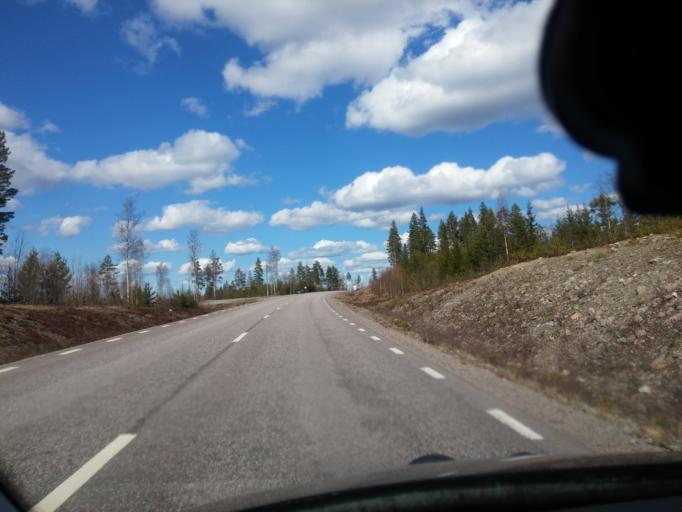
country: SE
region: Gaevleborg
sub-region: Ovanakers Kommun
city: Edsbyn
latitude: 61.2376
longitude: 15.8811
